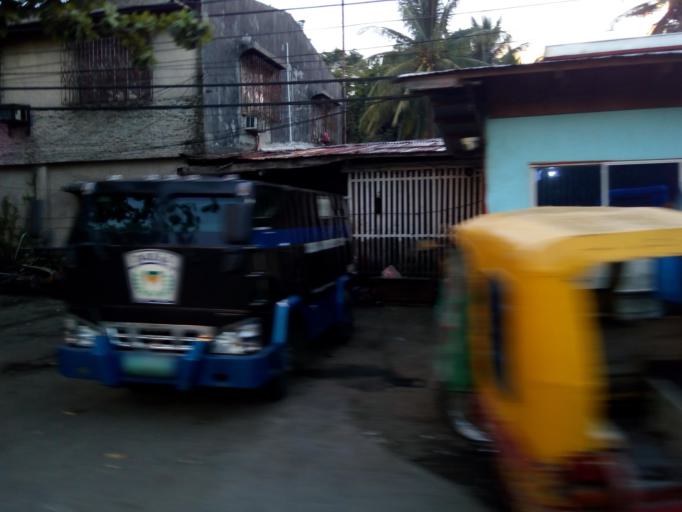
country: PH
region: Caraga
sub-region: Province of Surigao del Norte
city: Surigao
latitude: 9.7773
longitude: 125.4819
